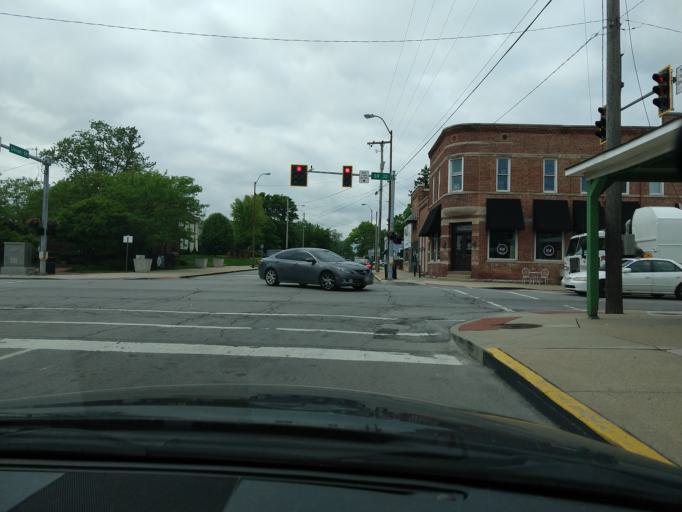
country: US
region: Indiana
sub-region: Hamilton County
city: Westfield
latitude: 40.0425
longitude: -86.1277
